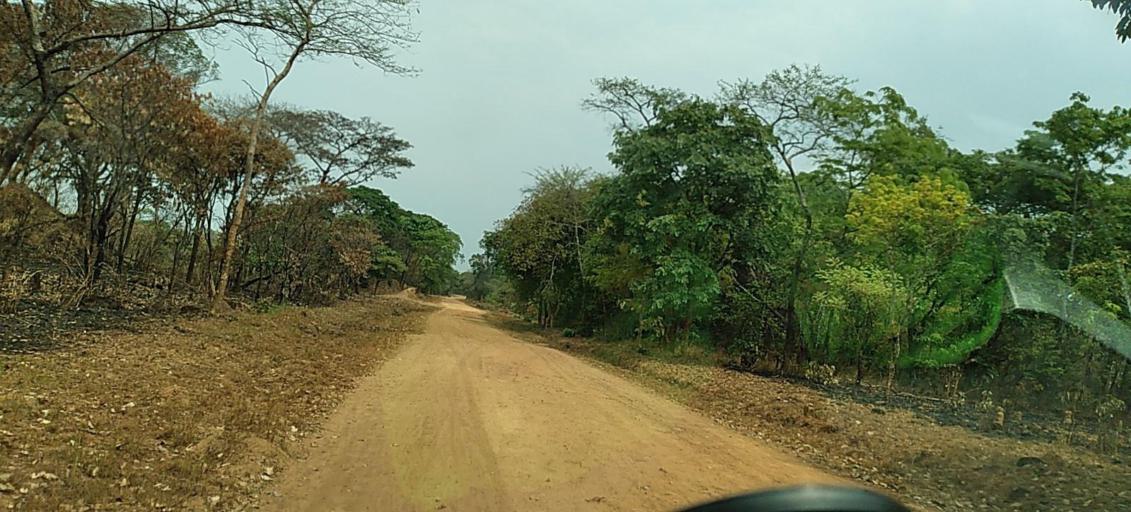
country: ZM
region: North-Western
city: Solwezi
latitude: -12.9586
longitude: 26.5668
